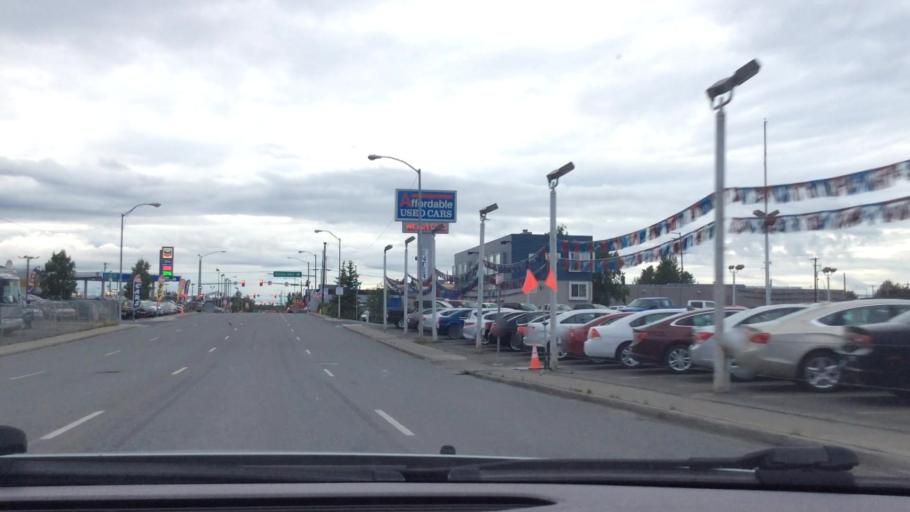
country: US
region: Alaska
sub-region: Anchorage Municipality
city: Anchorage
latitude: 61.2149
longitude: -149.8669
